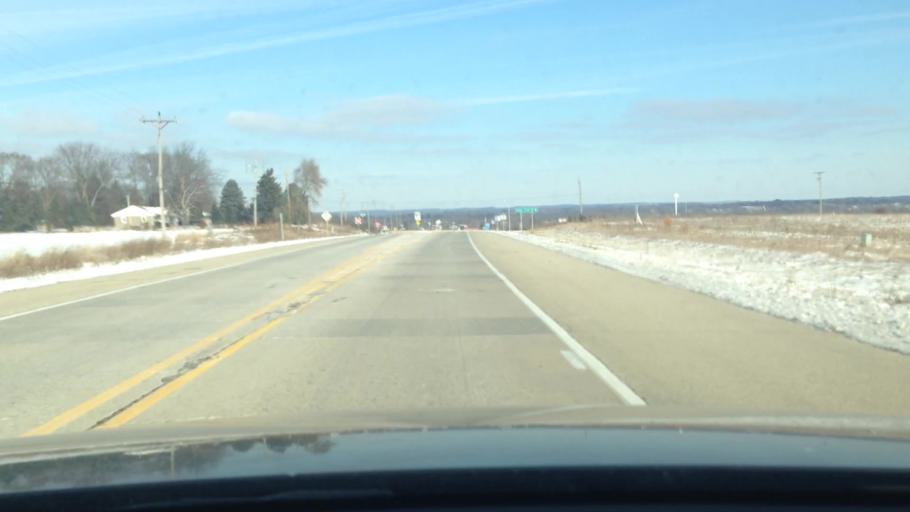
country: US
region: Wisconsin
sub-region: Walworth County
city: East Troy
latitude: 42.7682
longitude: -88.4063
